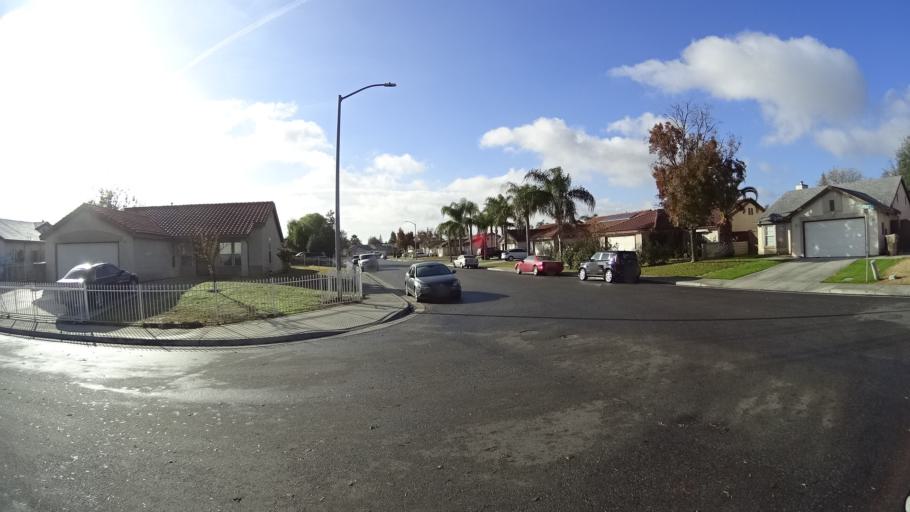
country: US
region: California
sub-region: Kern County
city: Greenfield
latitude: 35.2909
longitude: -119.0107
